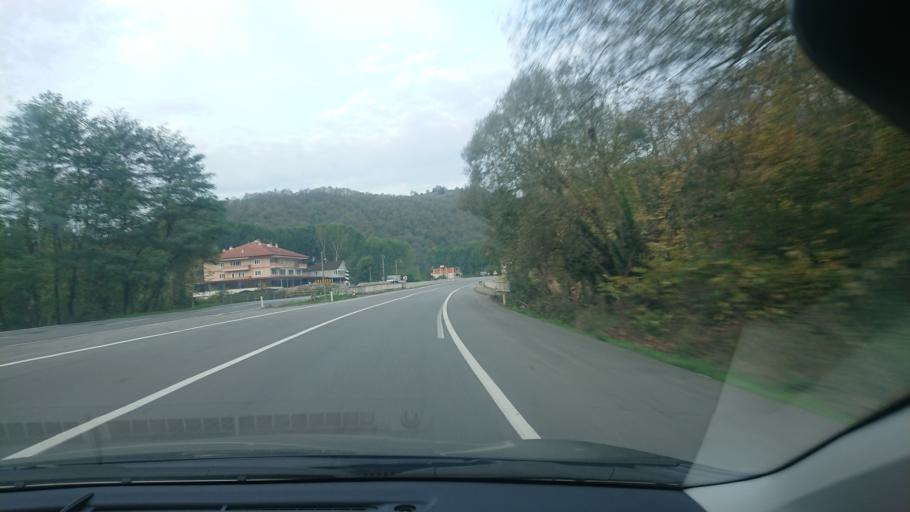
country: TR
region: Zonguldak
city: Beycuma
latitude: 41.3242
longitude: 32.0522
